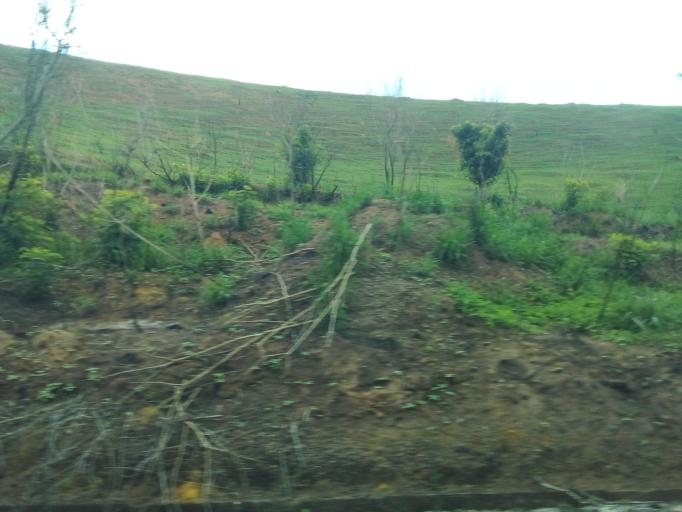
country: BR
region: Minas Gerais
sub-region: Governador Valadares
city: Governador Valadares
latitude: -19.0766
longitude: -42.1574
